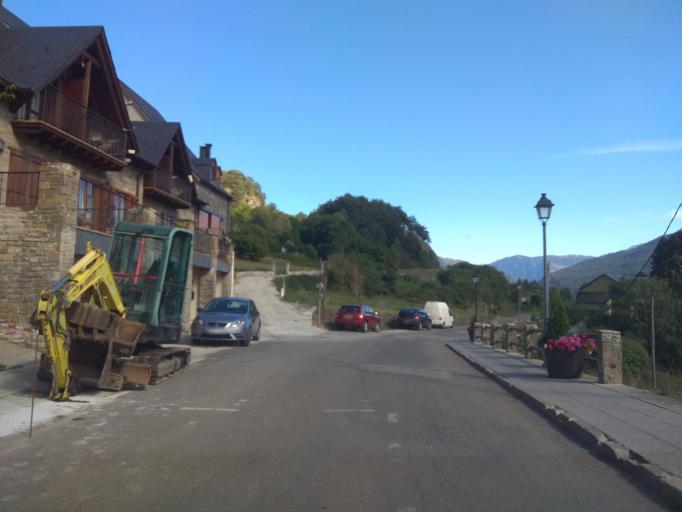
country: ES
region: Catalonia
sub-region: Provincia de Lleida
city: Les
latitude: 42.7474
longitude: 0.7279
